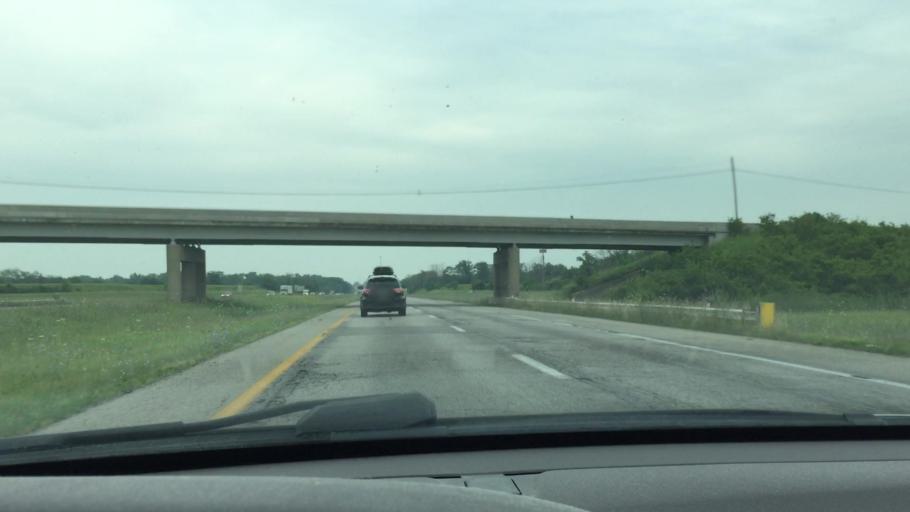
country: US
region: Ohio
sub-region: Madison County
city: Mount Sterling
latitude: 39.7572
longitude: -83.3017
